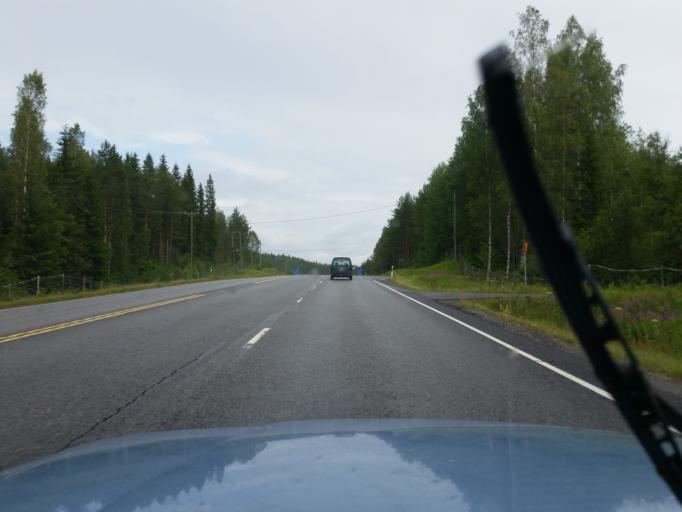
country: FI
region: Southern Savonia
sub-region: Mikkeli
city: Pertunmaa
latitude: 61.4368
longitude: 26.5078
